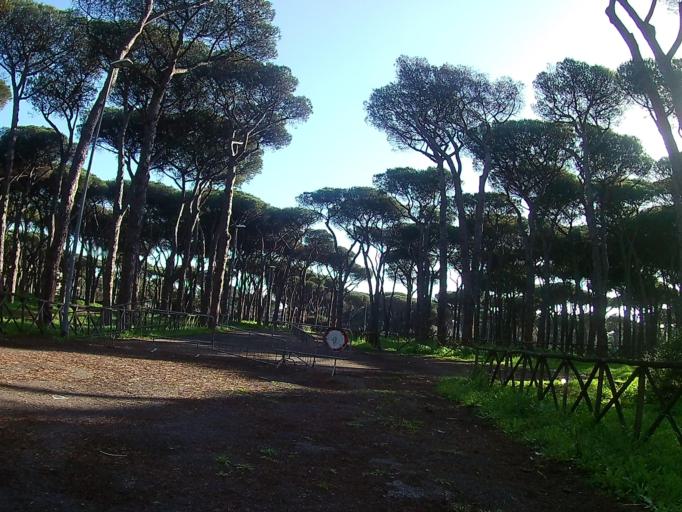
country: IT
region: Latium
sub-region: Citta metropolitana di Roma Capitale
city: Lido di Ostia
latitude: 41.7327
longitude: 12.2972
